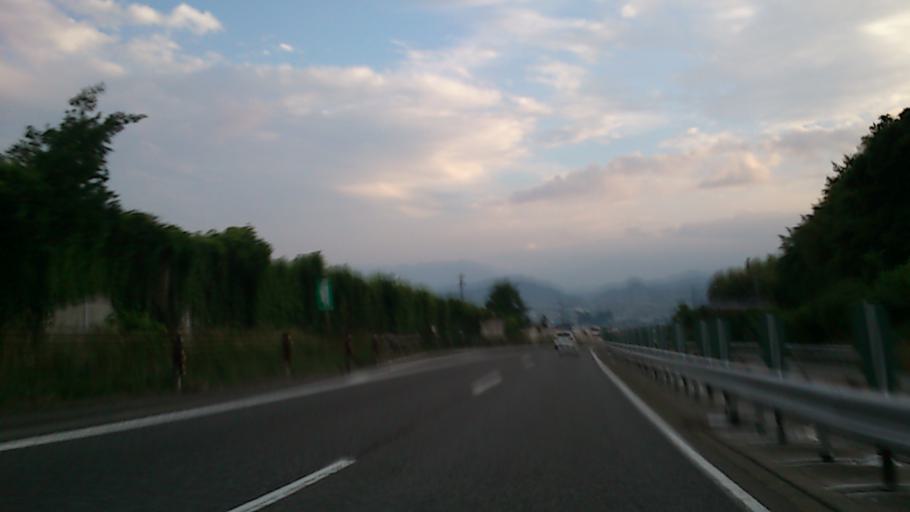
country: JP
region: Nagano
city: Iida
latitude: 35.5287
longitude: 137.8255
